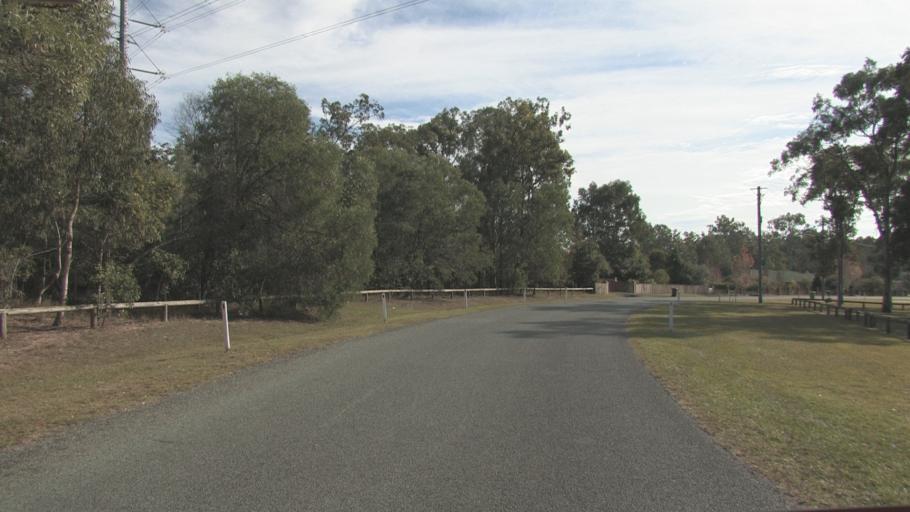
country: AU
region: Queensland
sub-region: Logan
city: Park Ridge South
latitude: -27.7345
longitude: 153.0297
